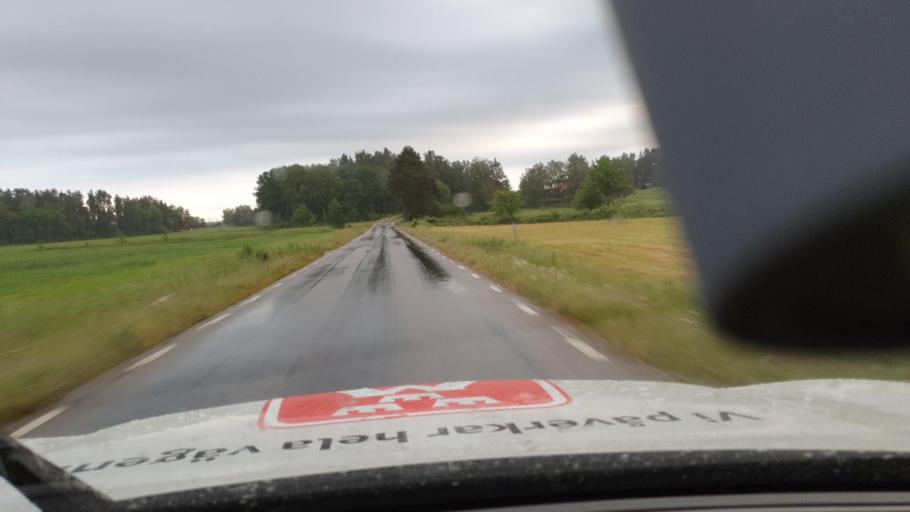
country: SE
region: Vaestra Goetaland
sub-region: Skovde Kommun
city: Stopen
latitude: 58.5472
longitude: 13.8661
